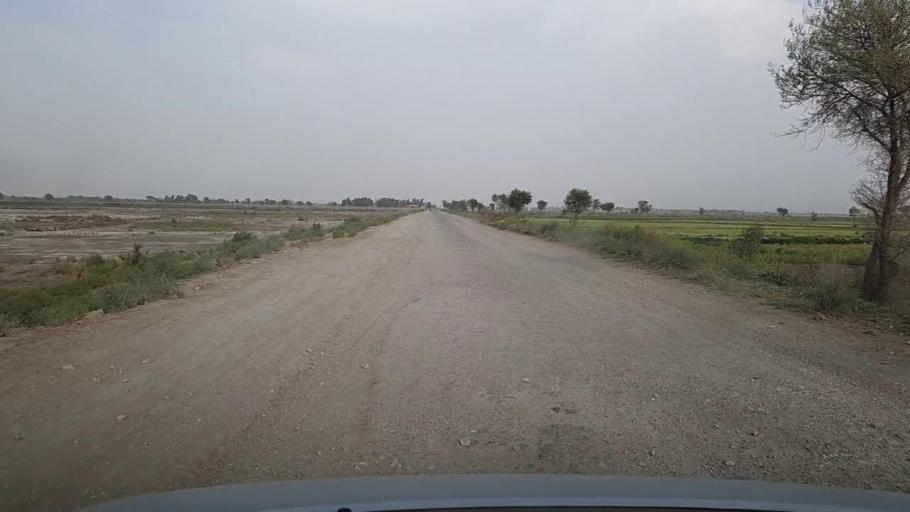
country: PK
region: Sindh
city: Dadu
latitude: 26.8147
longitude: 67.7721
